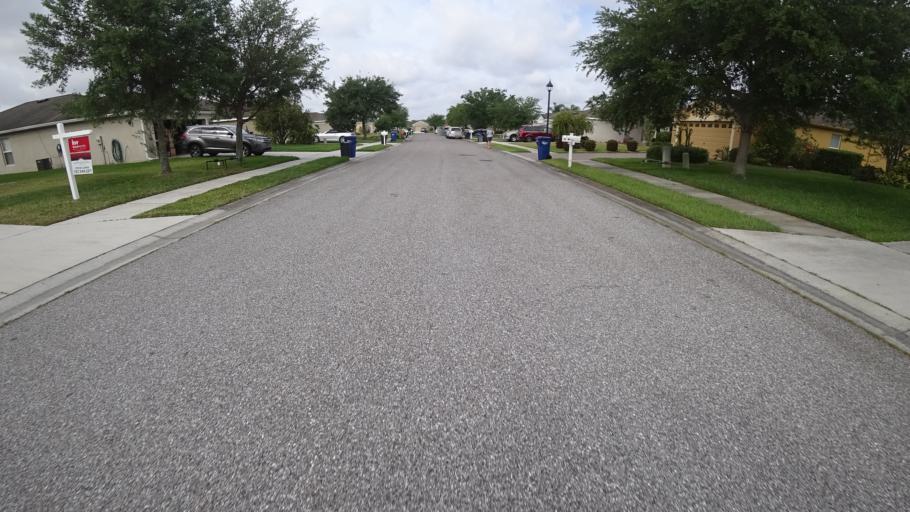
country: US
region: Florida
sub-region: Manatee County
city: Ellenton
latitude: 27.5601
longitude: -82.4617
